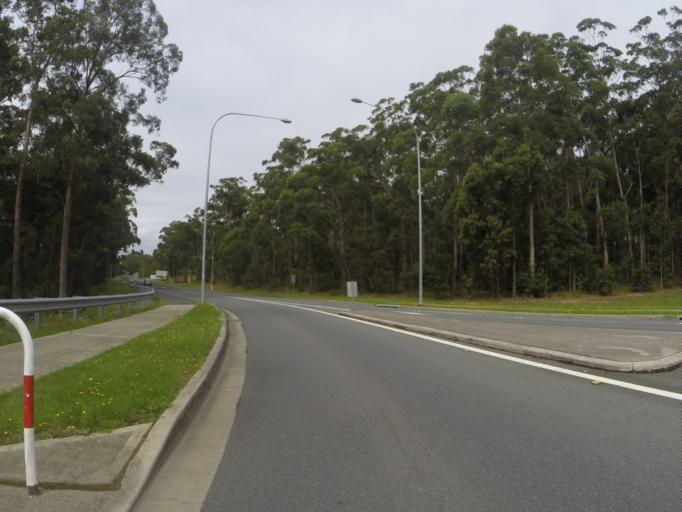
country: AU
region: New South Wales
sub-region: Eurobodalla
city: Batemans Bay
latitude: -35.7450
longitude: 150.2015
